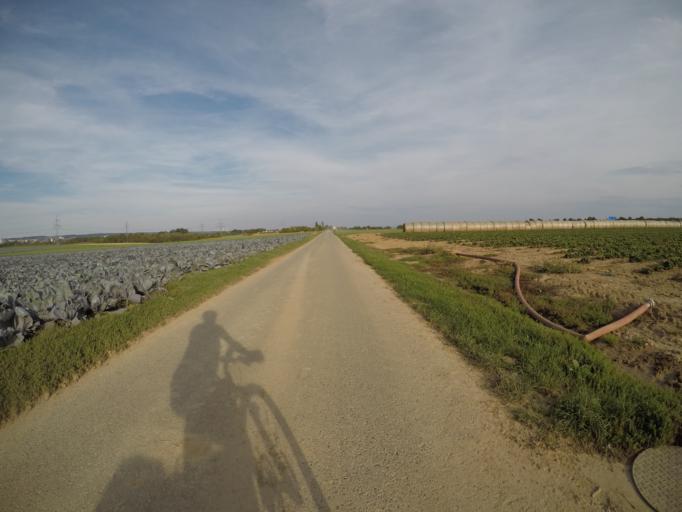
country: DE
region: Baden-Wuerttemberg
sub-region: Regierungsbezirk Stuttgart
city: Neuhausen auf den Fildern
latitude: 48.6980
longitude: 9.2723
